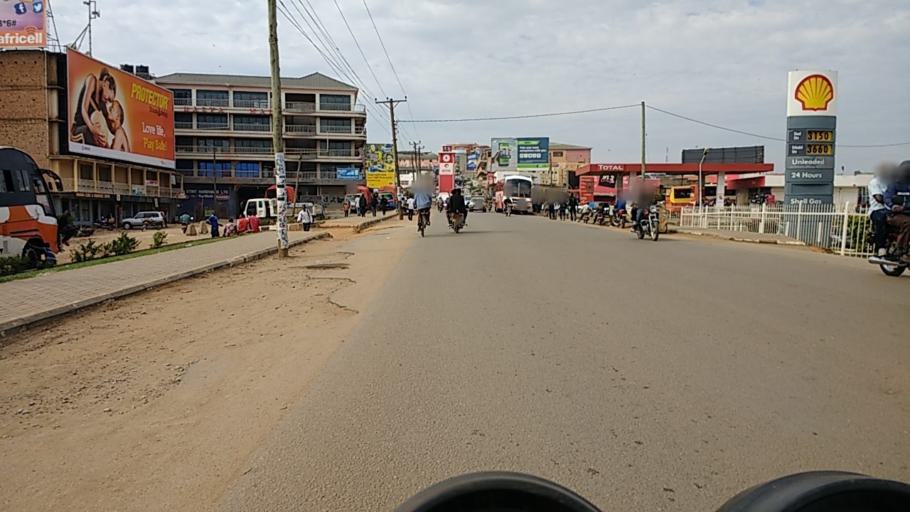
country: UG
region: Western Region
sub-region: Mbarara District
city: Mbarara
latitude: -0.6015
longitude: 30.6634
